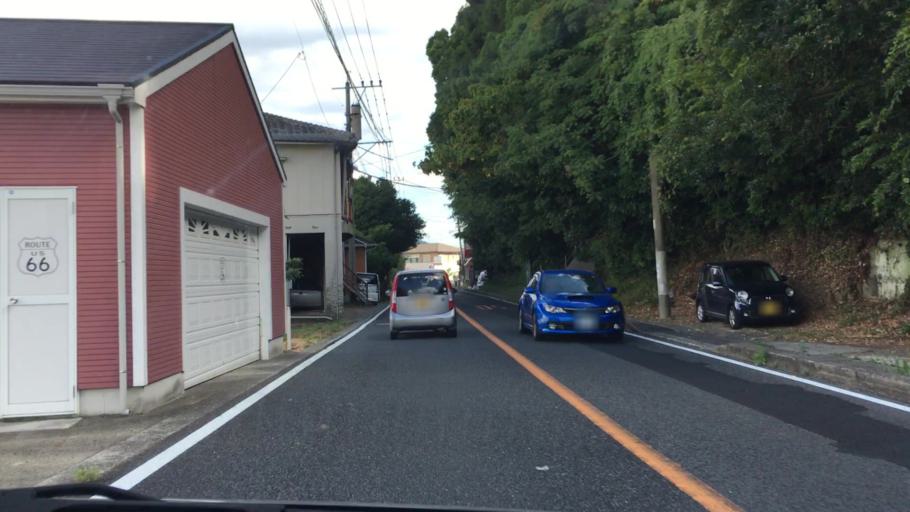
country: JP
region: Nagasaki
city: Sasebo
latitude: 33.1349
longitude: 129.7952
